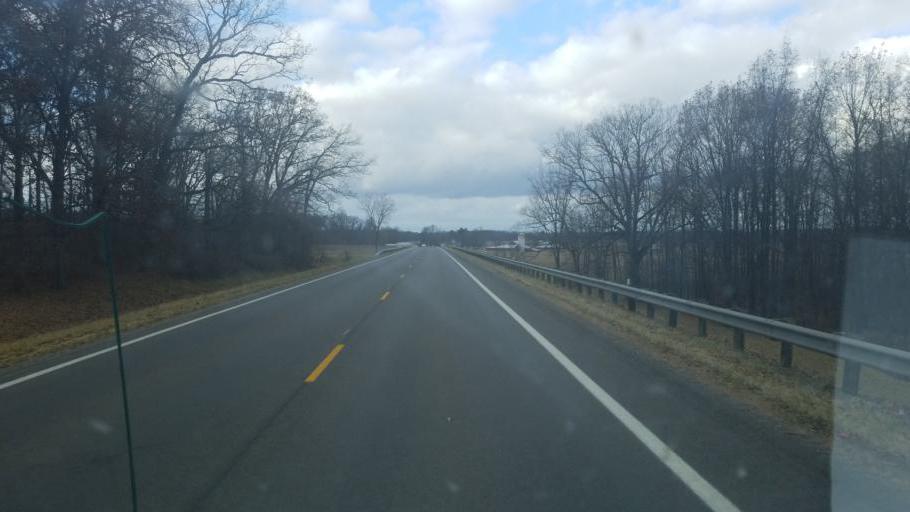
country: US
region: Ohio
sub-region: Wyandot County
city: Upper Sandusky
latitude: 40.7899
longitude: -83.2602
